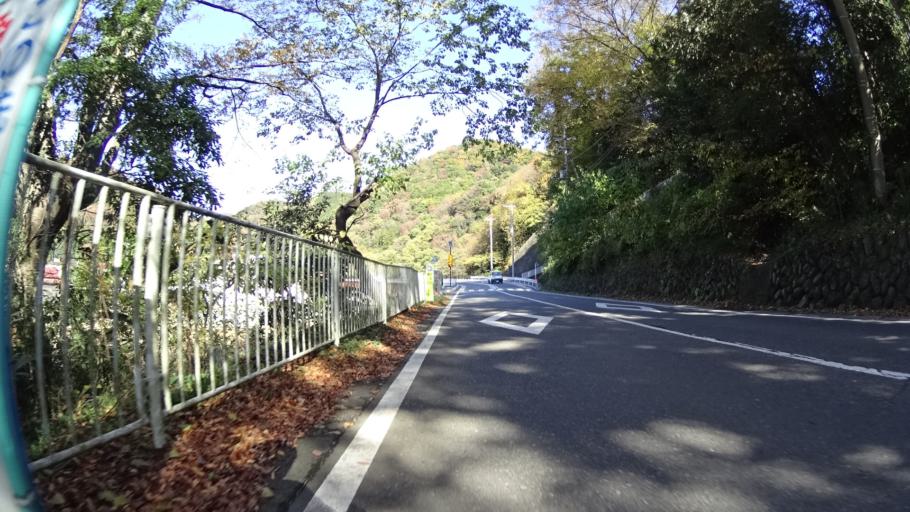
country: JP
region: Kanagawa
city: Zama
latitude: 35.5308
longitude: 139.2854
